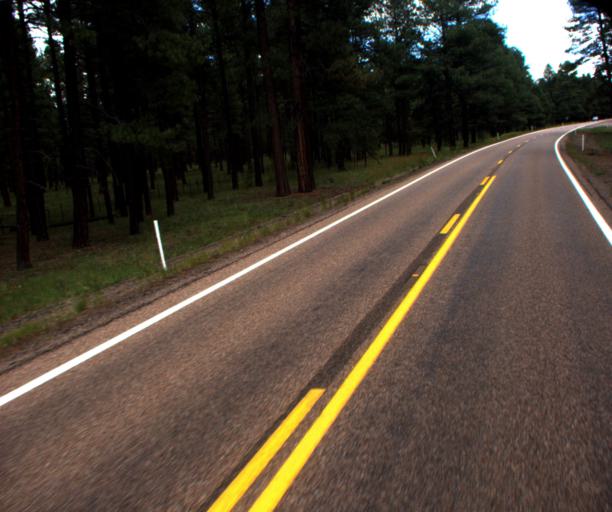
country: US
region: Arizona
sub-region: Navajo County
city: Pinetop-Lakeside
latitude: 34.0796
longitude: -109.8014
